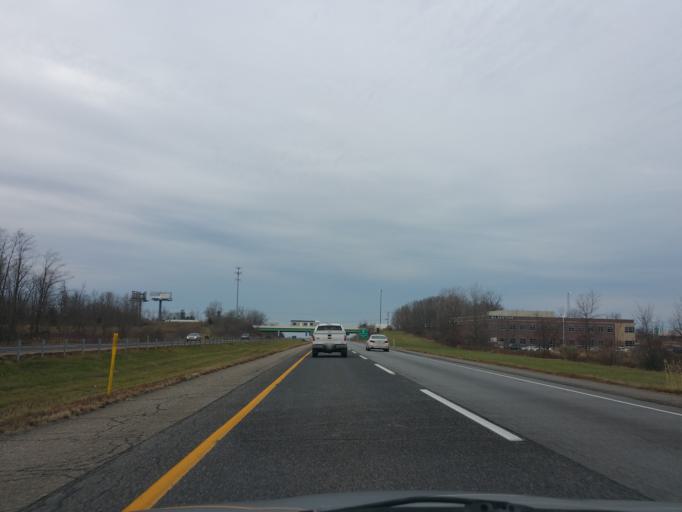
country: US
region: Indiana
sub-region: Porter County
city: Chesterton
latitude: 41.5728
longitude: -87.0407
